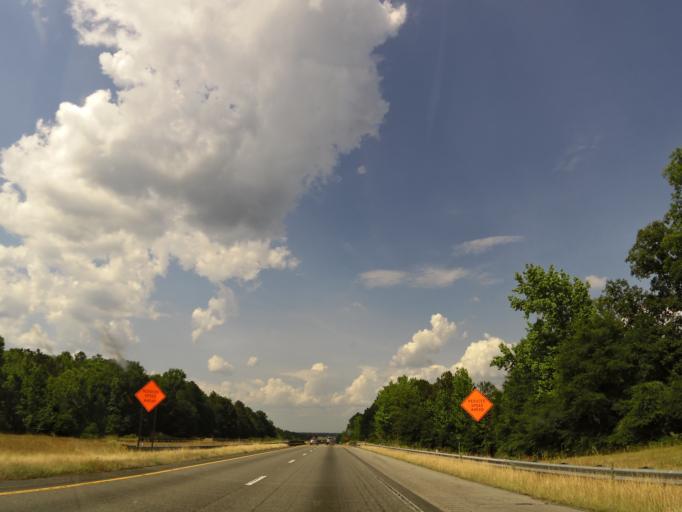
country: US
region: Alabama
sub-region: Hale County
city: Moundville
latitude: 33.0677
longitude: -87.6950
